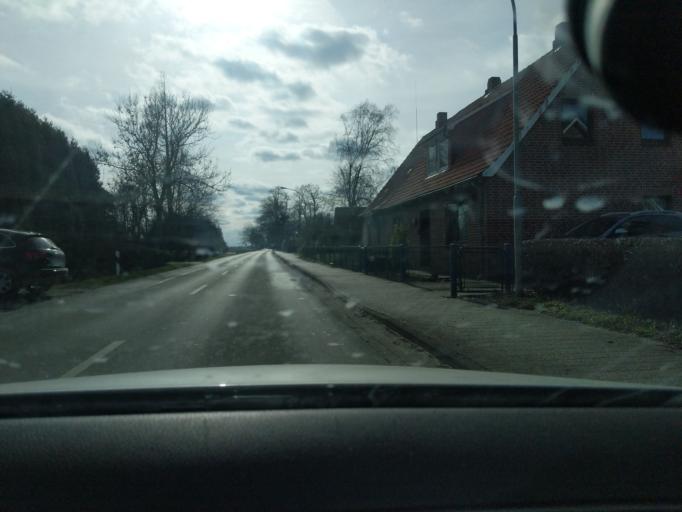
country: DE
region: Lower Saxony
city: Drochtersen
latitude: 53.6955
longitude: 9.4082
